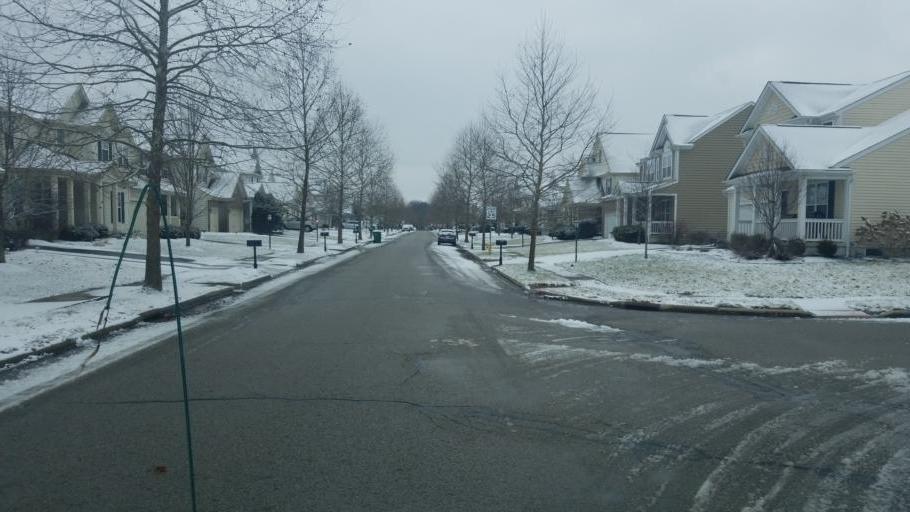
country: US
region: Ohio
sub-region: Franklin County
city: Reynoldsburg
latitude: 40.0151
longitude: -82.7947
